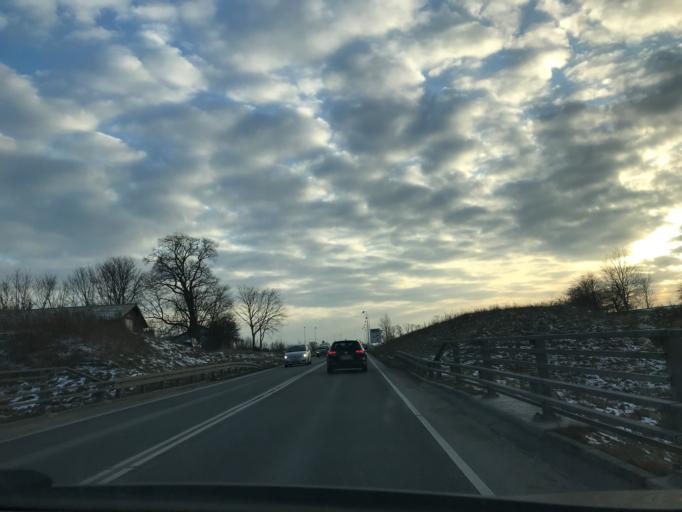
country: DK
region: Capital Region
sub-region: Egedal Kommune
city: Smorumnedre
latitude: 55.7207
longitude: 12.3143
